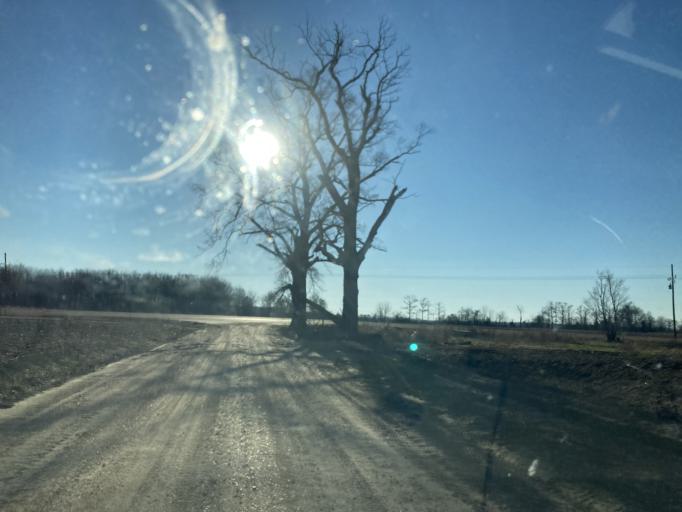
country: US
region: Mississippi
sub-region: Yazoo County
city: Yazoo City
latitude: 32.9224
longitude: -90.6095
